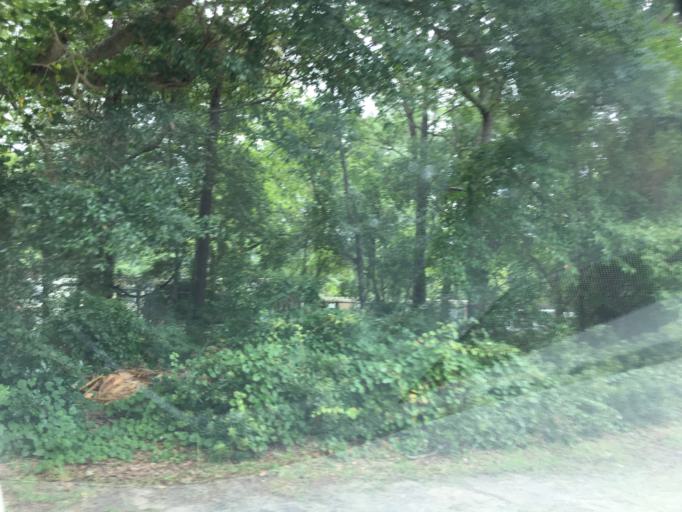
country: US
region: South Carolina
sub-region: Horry County
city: North Myrtle Beach
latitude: 33.7767
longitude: -78.7749
